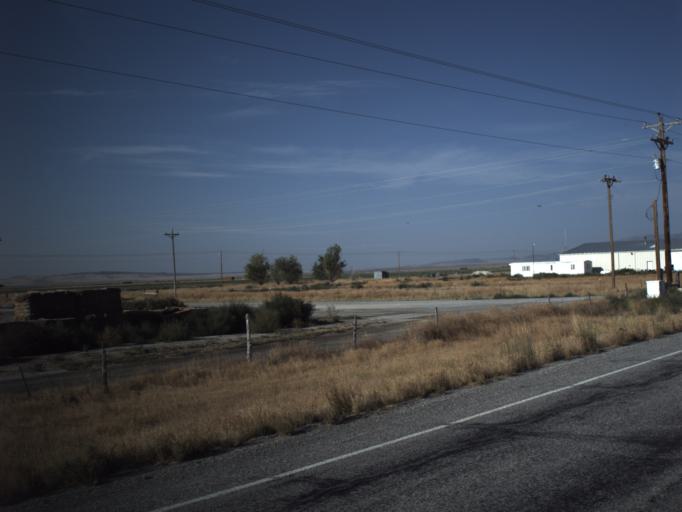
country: US
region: Idaho
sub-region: Oneida County
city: Malad City
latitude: 41.9667
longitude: -112.9014
